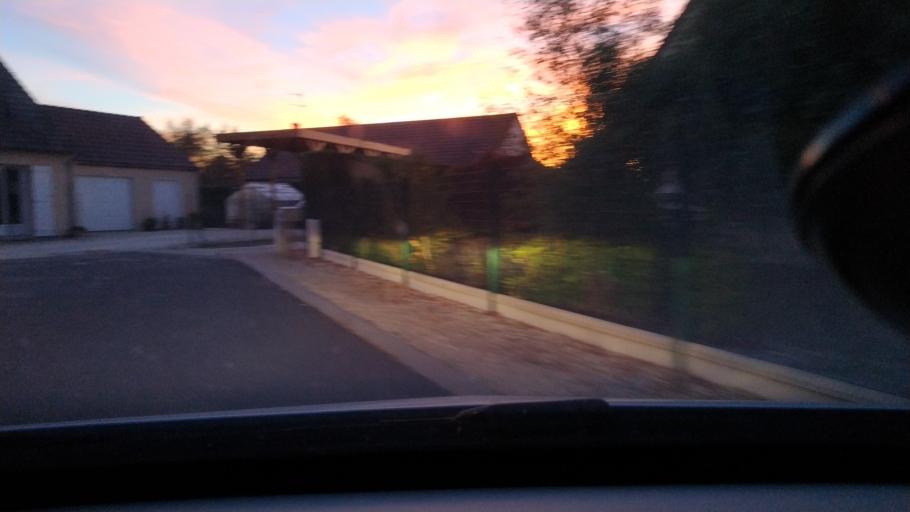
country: FR
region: Centre
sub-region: Departement du Cher
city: Brinon-sur-Sauldre
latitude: 47.6107
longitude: 2.1677
